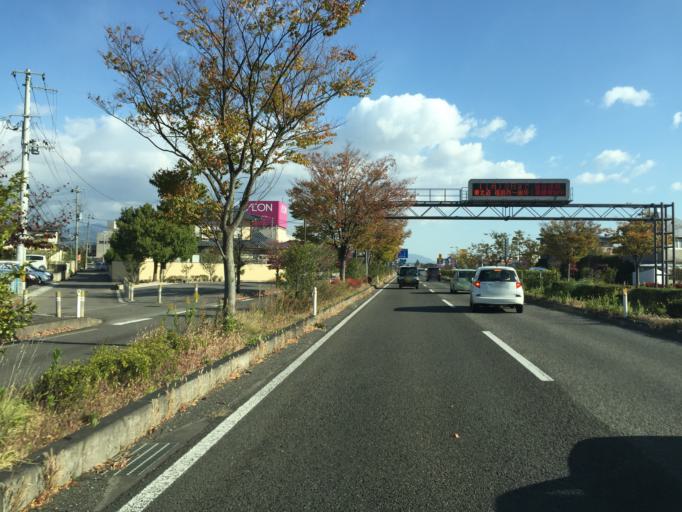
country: JP
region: Fukushima
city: Fukushima-shi
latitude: 37.7853
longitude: 140.4565
